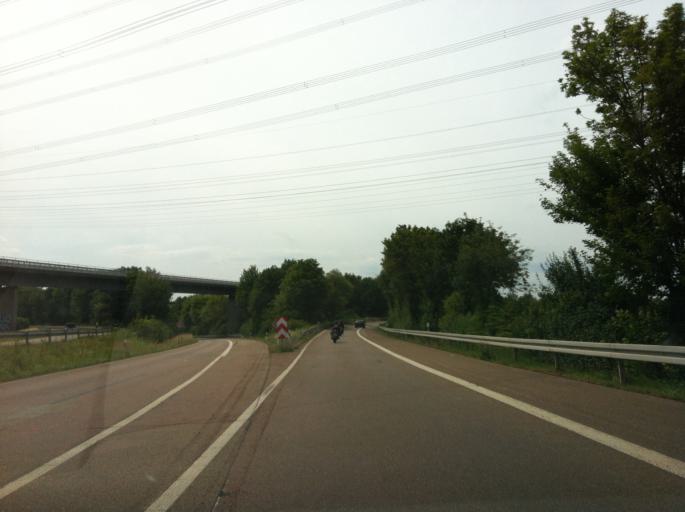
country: DE
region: Hesse
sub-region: Regierungsbezirk Darmstadt
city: Hattersheim
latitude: 50.0825
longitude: 8.4924
